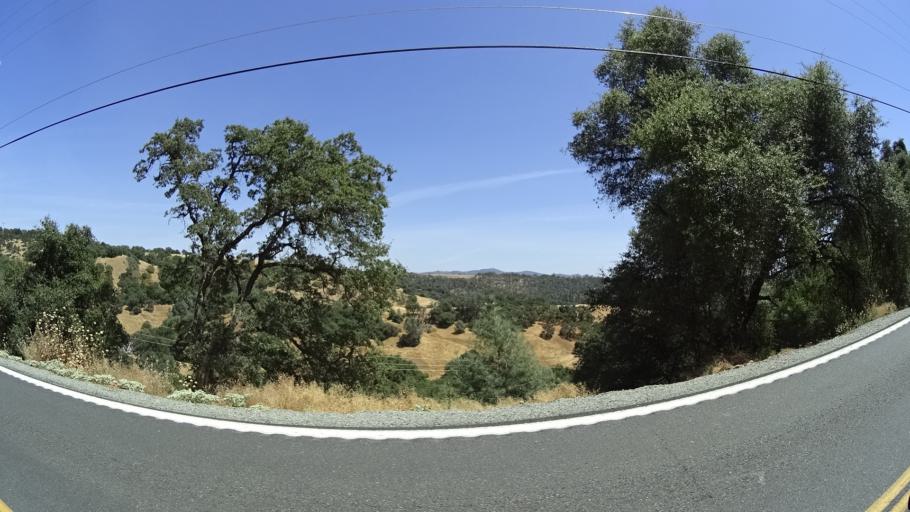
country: US
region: California
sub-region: Amador County
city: Jackson
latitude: 38.2937
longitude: -120.7069
